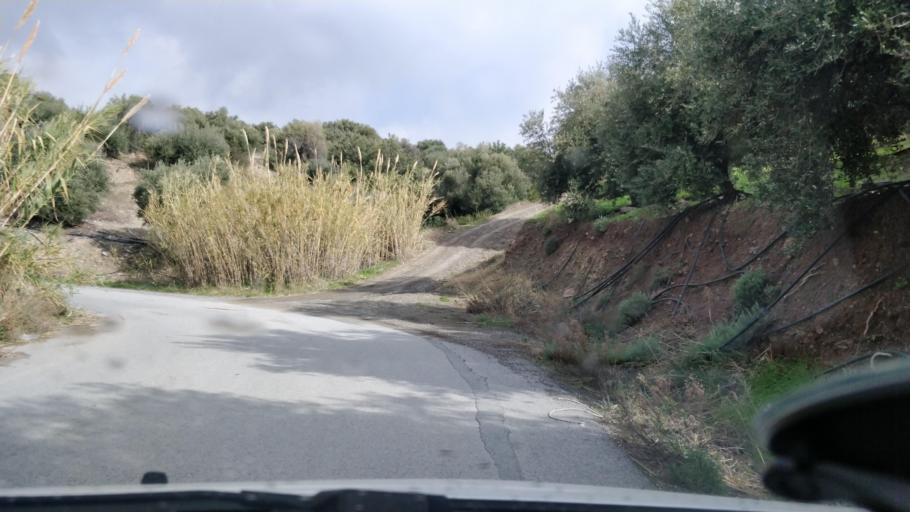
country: GR
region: Crete
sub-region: Nomos Lasithiou
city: Gra Liyia
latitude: 34.9963
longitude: 25.5131
